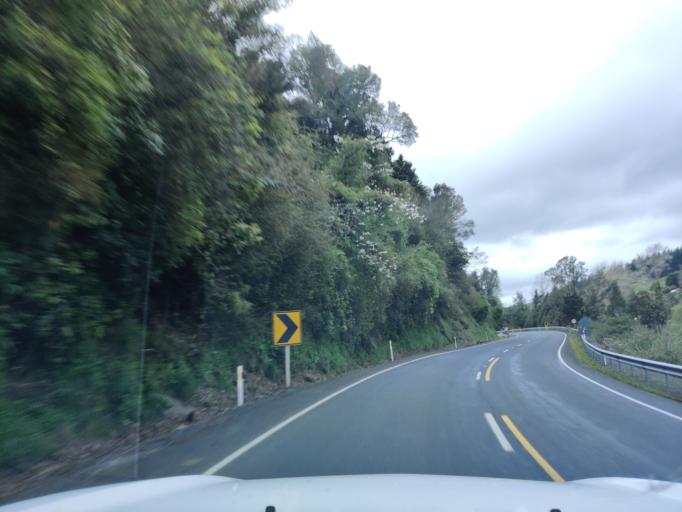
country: NZ
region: Waikato
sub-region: Otorohanga District
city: Otorohanga
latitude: -38.6089
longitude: 175.2167
